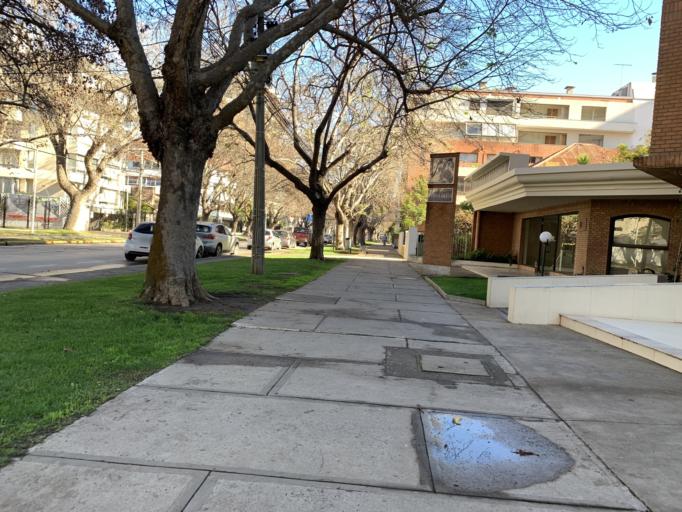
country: CL
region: Valparaiso
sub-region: Provincia de Valparaiso
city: Vina del Mar
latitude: -33.0156
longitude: -71.5476
